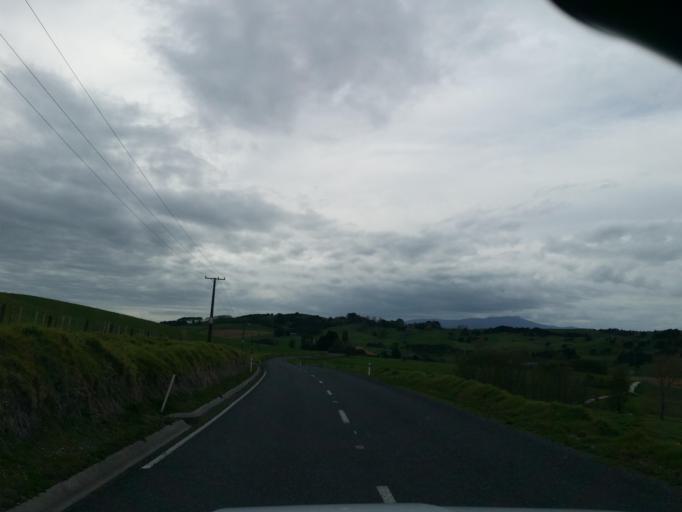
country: NZ
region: Northland
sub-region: Kaipara District
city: Dargaville
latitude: -35.9734
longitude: 173.9469
